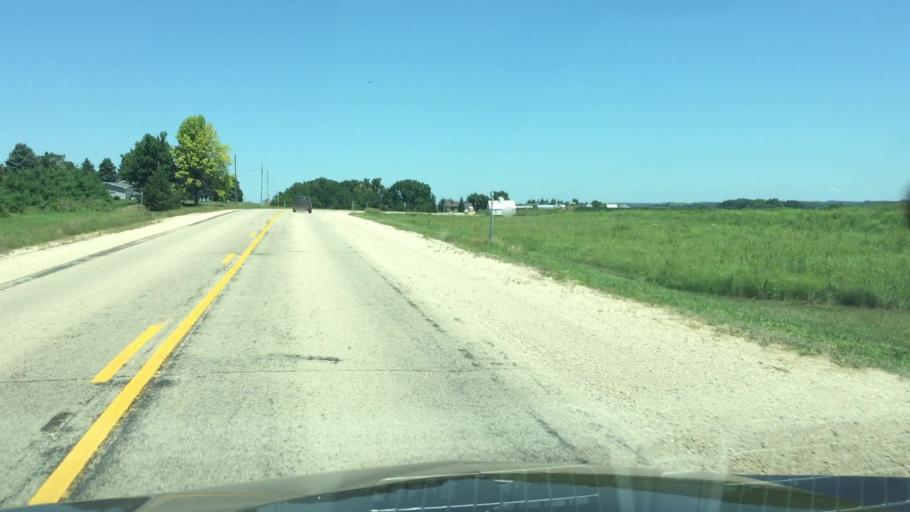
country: US
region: Iowa
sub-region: Cedar County
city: Mechanicsville
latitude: 41.9579
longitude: -91.1519
